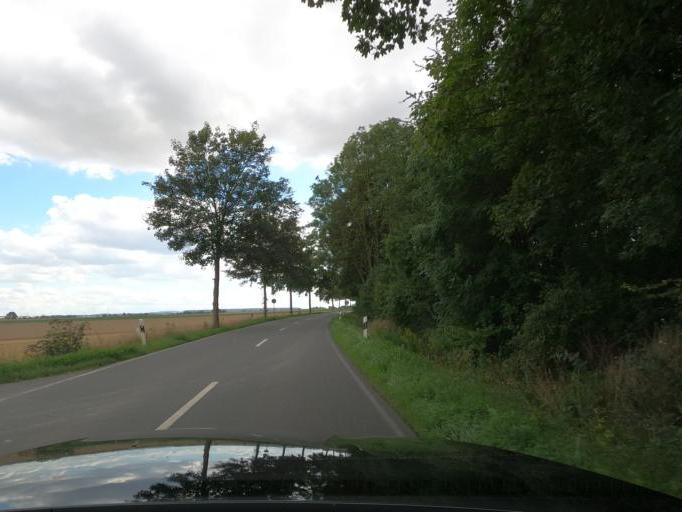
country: DE
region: Lower Saxony
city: Ilsede
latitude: 52.2281
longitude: 10.1747
